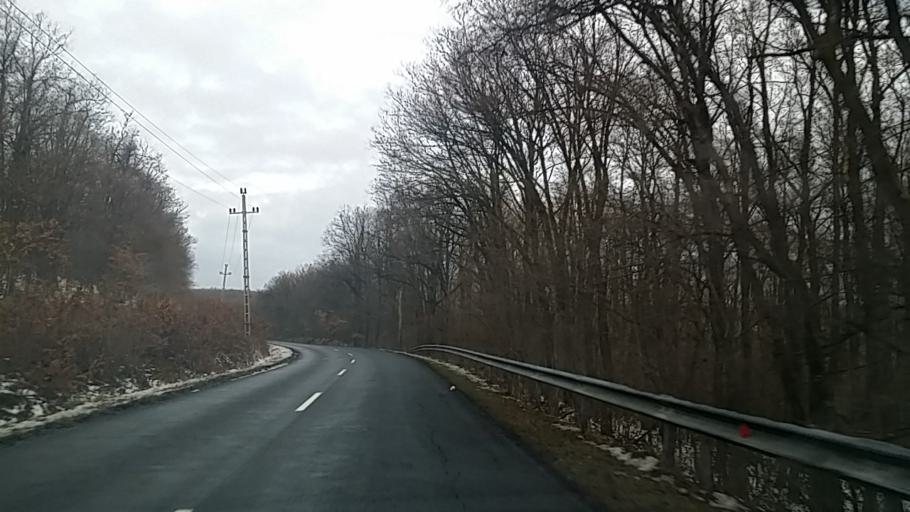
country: HU
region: Pest
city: Nagykovacsi
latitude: 47.7165
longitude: 19.0116
